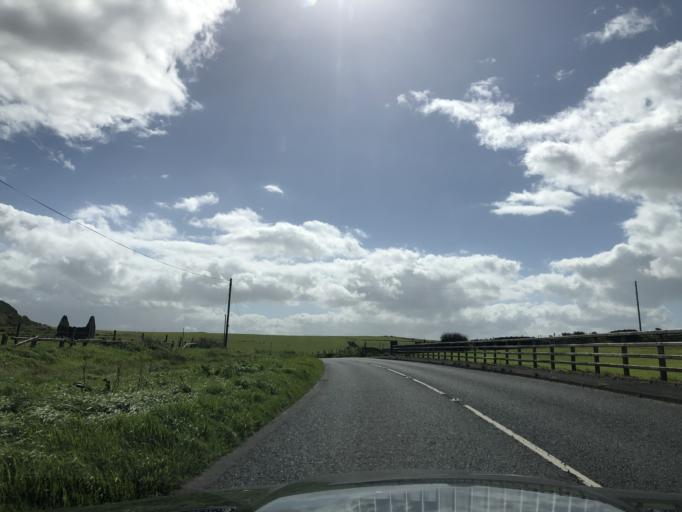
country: GB
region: Northern Ireland
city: Bushmills
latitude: 55.2133
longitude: -6.5653
